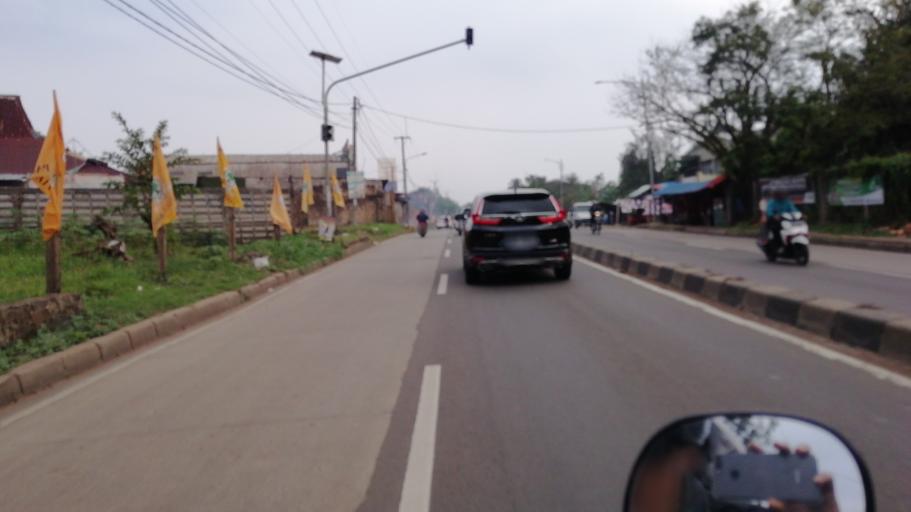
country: ID
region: West Java
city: Parung
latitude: -6.4965
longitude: 106.7535
